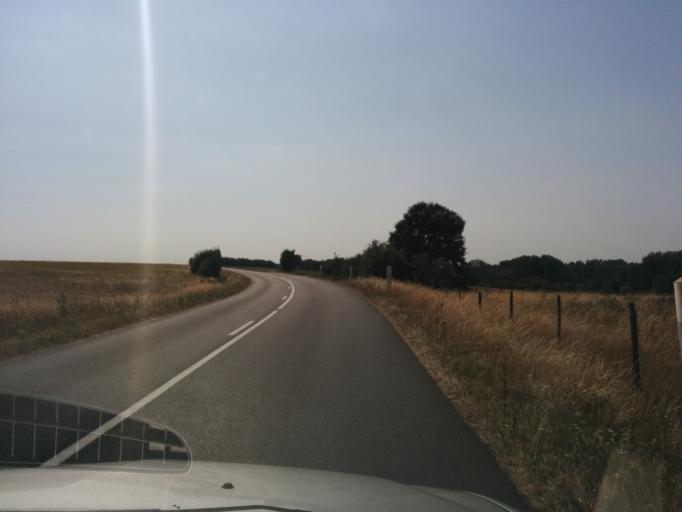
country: FR
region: Poitou-Charentes
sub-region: Departement de la Vienne
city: Moncontour
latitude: 46.8088
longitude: -0.0039
